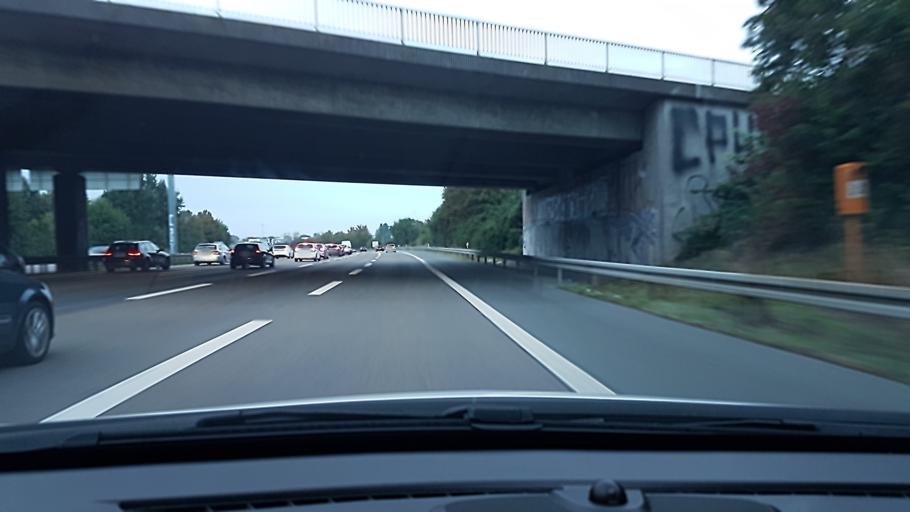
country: DE
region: Hesse
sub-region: Regierungsbezirk Darmstadt
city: Frankfurt am Main
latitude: 50.1506
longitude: 8.7048
